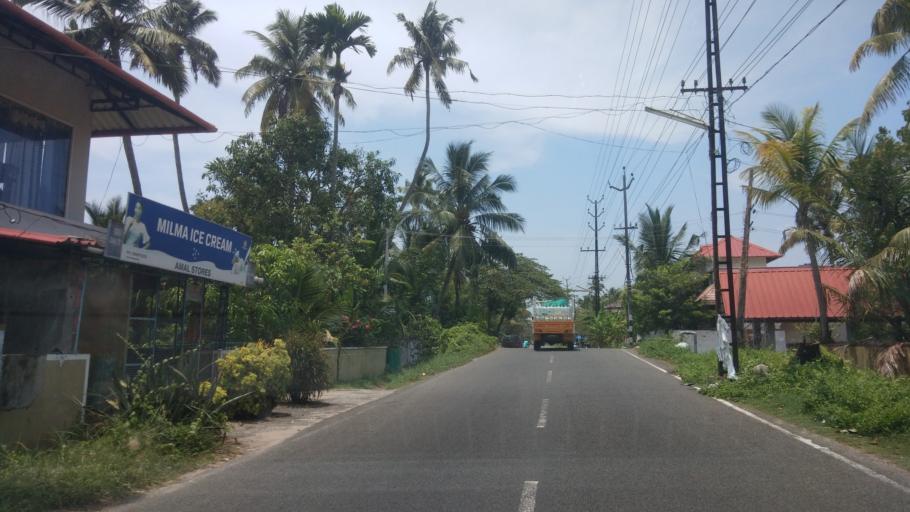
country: IN
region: Kerala
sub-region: Alappuzha
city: Kutiatodu
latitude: 9.8435
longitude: 76.2686
